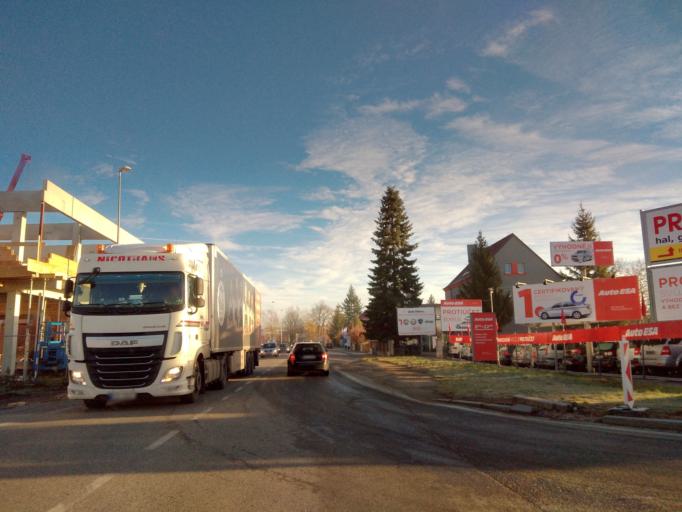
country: CZ
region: Jihocesky
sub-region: Okres Ceske Budejovice
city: Ceske Budejovice
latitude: 48.9809
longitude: 14.5027
